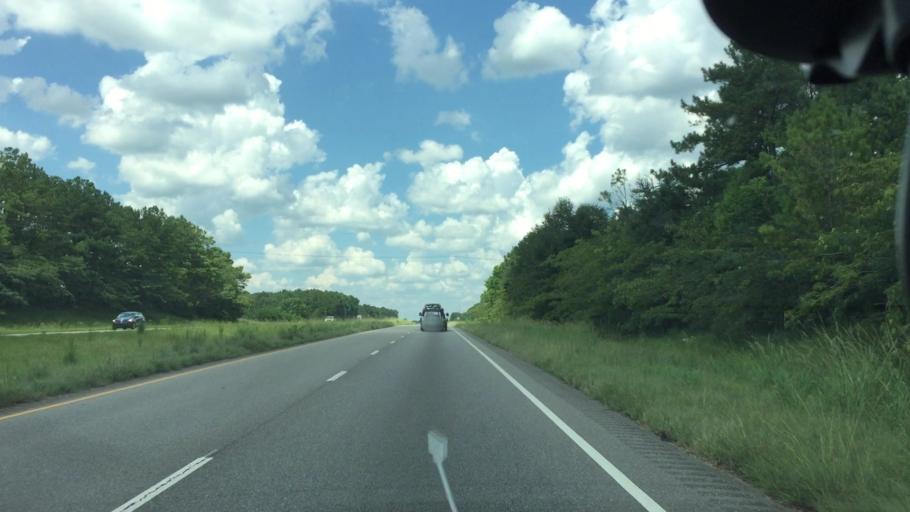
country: US
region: Alabama
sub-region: Montgomery County
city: Taylor
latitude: 32.0087
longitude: -86.0290
